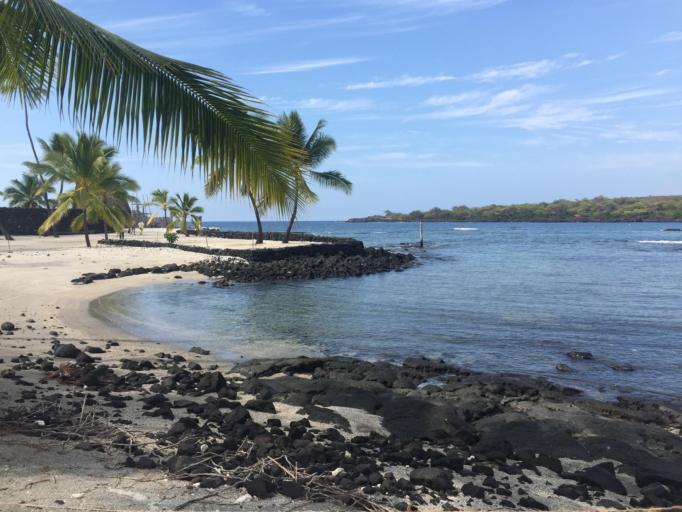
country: US
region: Hawaii
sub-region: Hawaii County
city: Honaunau-Napoopoo
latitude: 19.4214
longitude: -155.9113
